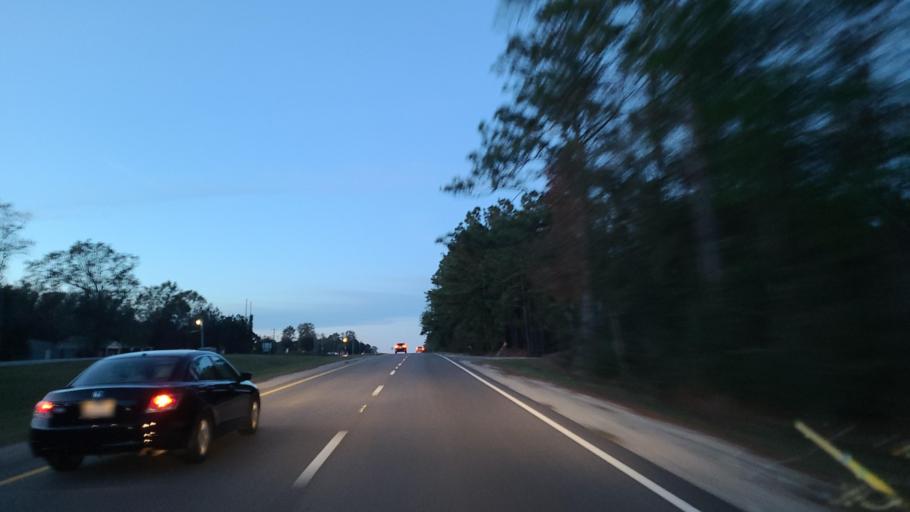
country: US
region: Mississippi
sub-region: Forrest County
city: Hattiesburg
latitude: 31.2181
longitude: -89.2645
